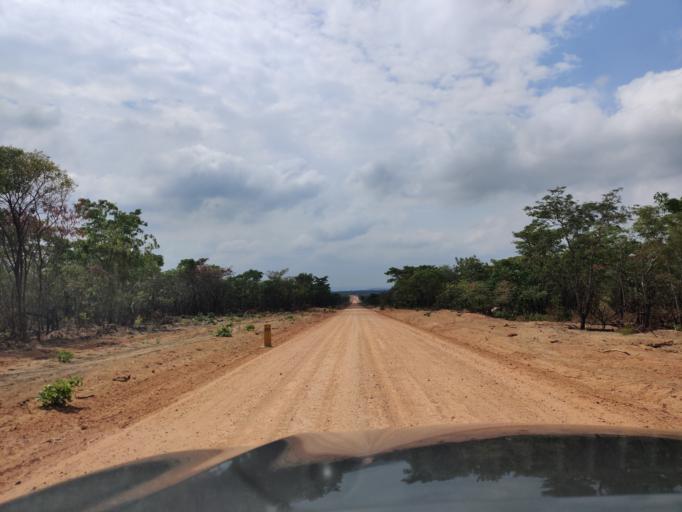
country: ZM
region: Central
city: Mkushi
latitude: -13.6746
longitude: 29.7524
